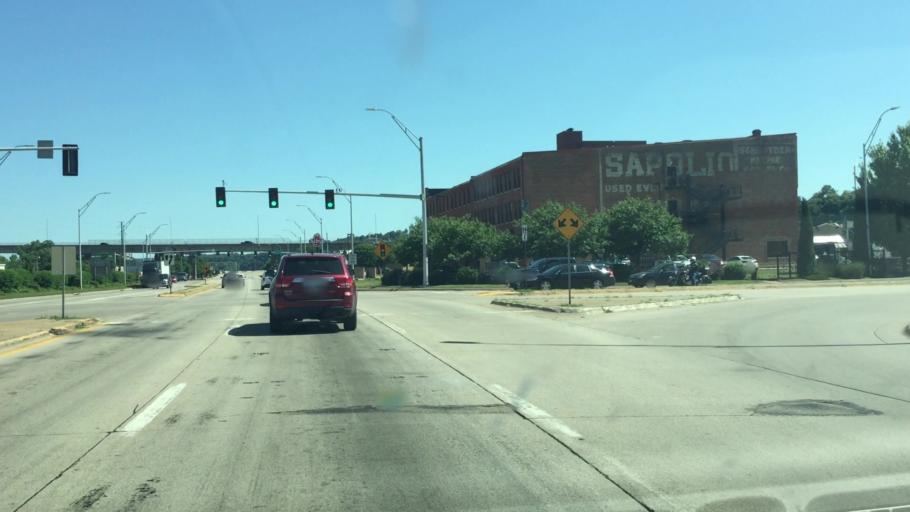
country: US
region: Iowa
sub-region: Dubuque County
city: Dubuque
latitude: 42.4947
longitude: -90.6630
